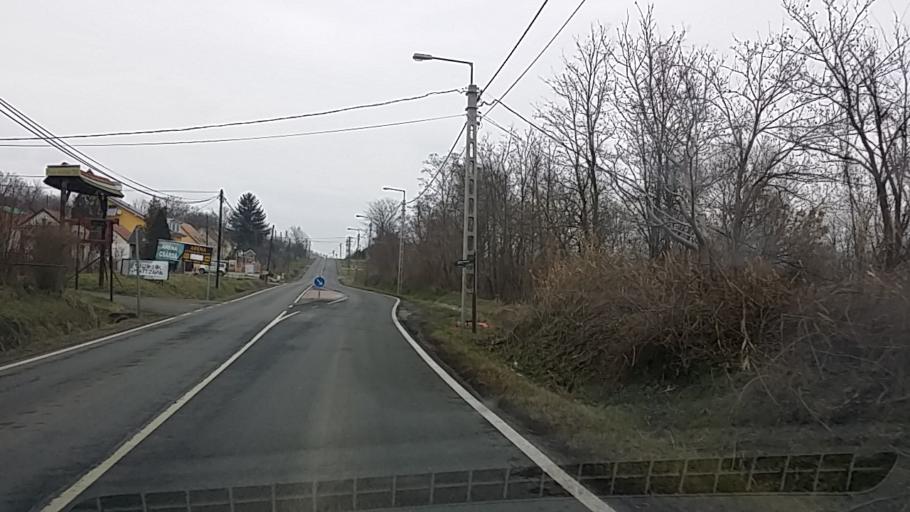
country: HU
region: Baranya
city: Dunaszekcso
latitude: 46.0697
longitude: 18.7524
